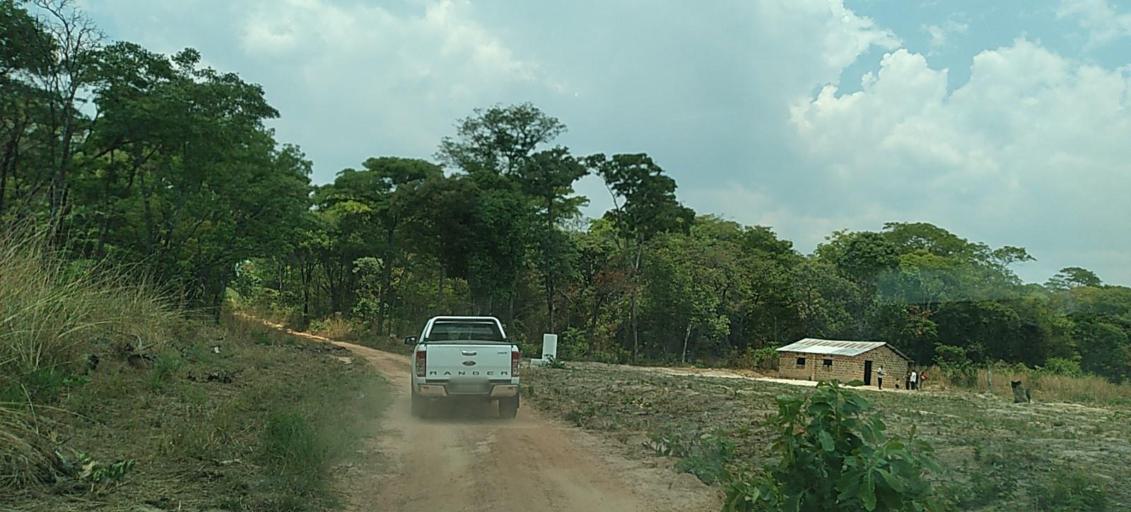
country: ZM
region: Copperbelt
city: Chingola
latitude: -12.7911
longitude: 27.6459
